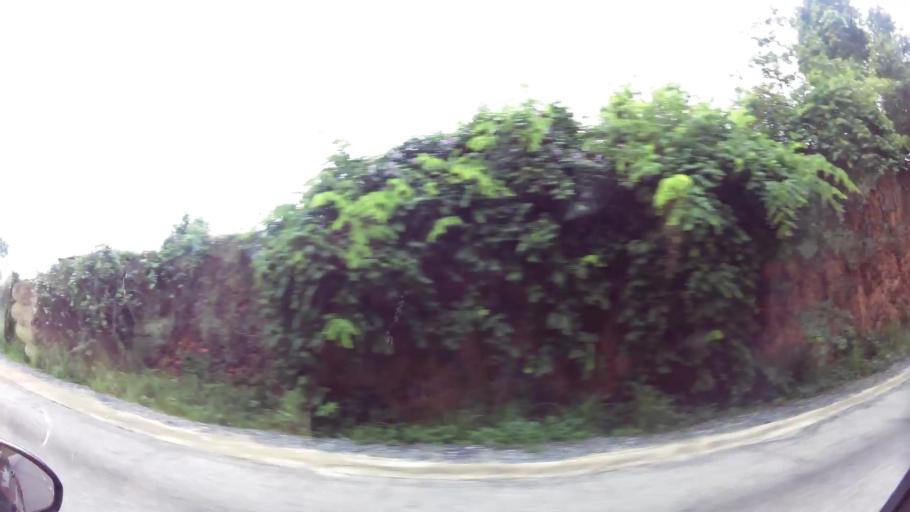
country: TT
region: City of Port of Spain
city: Port-of-Spain
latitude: 10.6752
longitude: -61.4990
